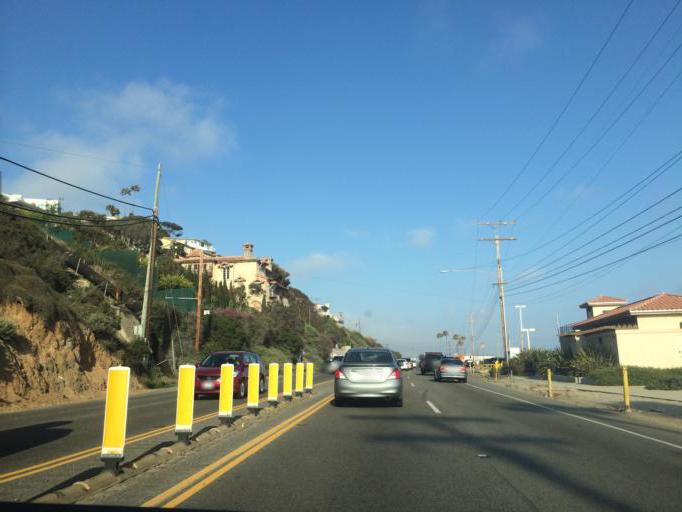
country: US
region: California
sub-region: Los Angeles County
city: Topanga
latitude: 34.0399
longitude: -118.5599
